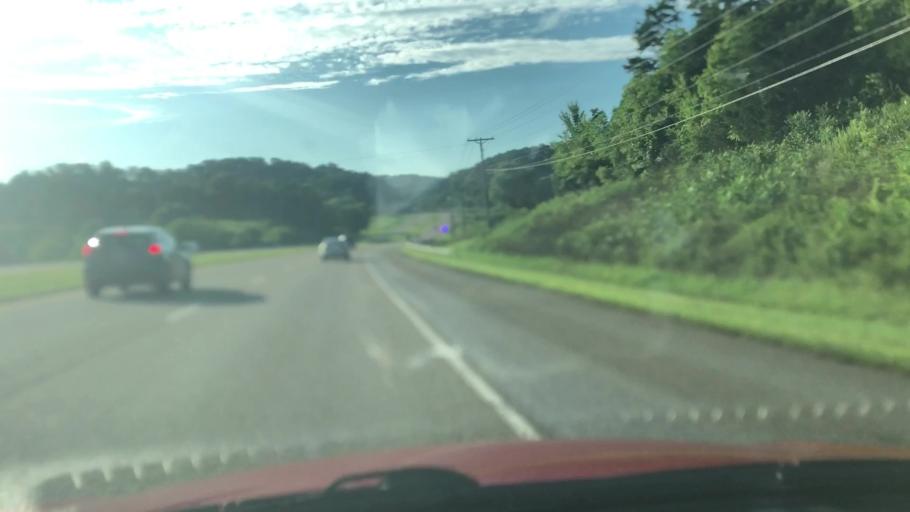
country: US
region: Tennessee
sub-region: Jefferson County
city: Dandridge
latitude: 36.0486
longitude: -83.4606
